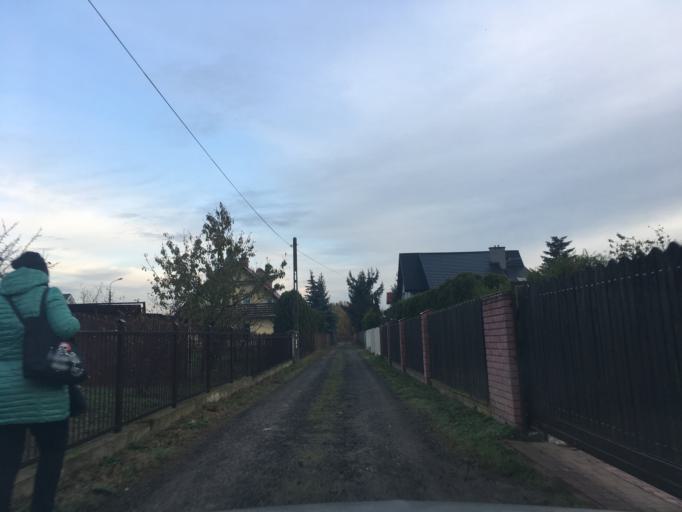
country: PL
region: Masovian Voivodeship
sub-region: Powiat pruszkowski
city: Brwinow
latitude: 52.1426
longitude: 20.7302
